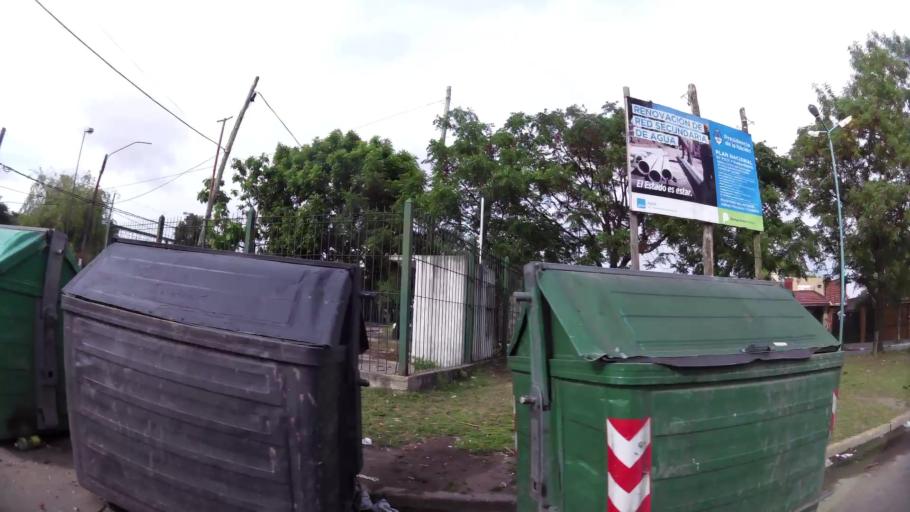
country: AR
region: Buenos Aires
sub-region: Partido de Quilmes
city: Quilmes
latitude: -34.7113
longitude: -58.2586
